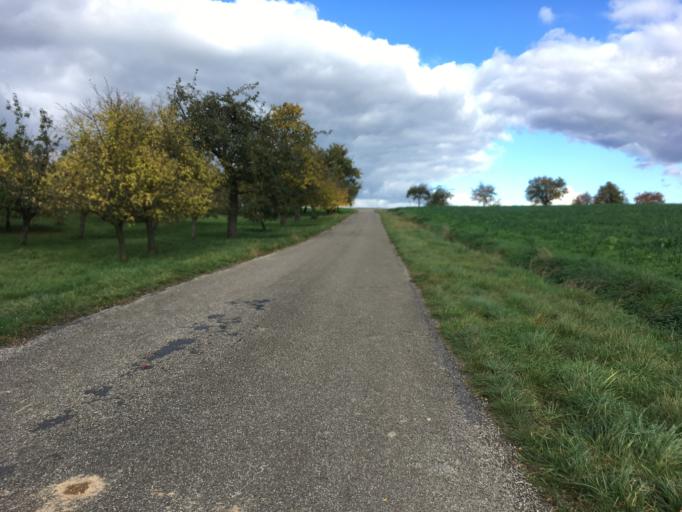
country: DE
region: Baden-Wuerttemberg
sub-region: Regierungsbezirk Stuttgart
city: Untermunkheim
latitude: 49.1843
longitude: 9.7094
